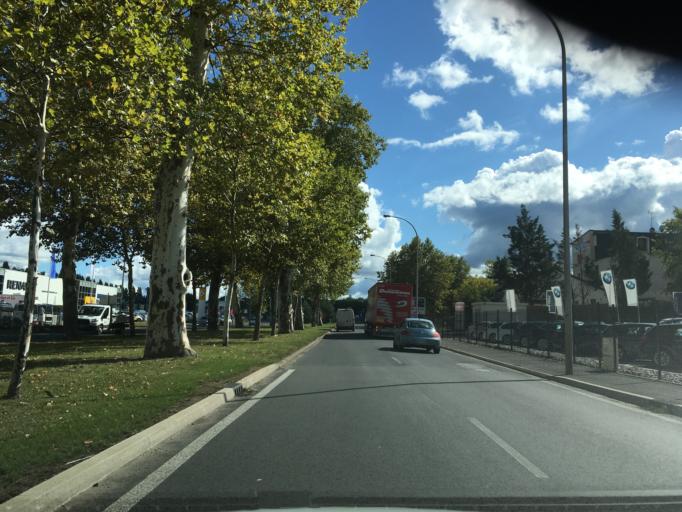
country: FR
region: Limousin
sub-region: Departement de la Correze
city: Saint-Pantaleon-de-Larche
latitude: 45.1485
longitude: 1.4820
